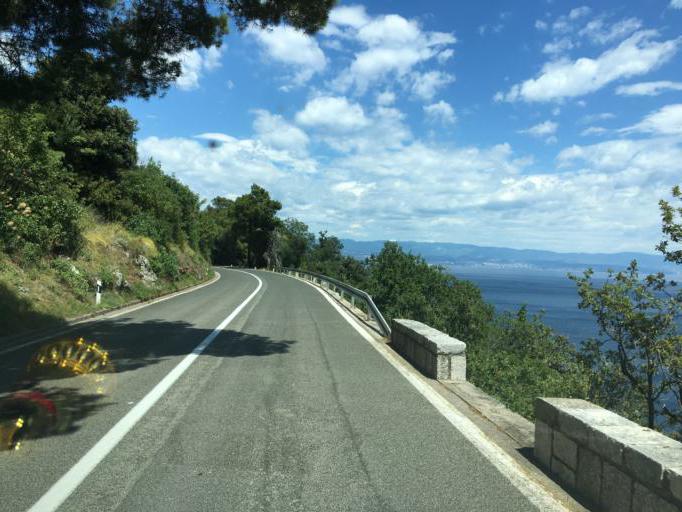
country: HR
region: Istarska
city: Lovran
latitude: 45.2153
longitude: 14.2480
